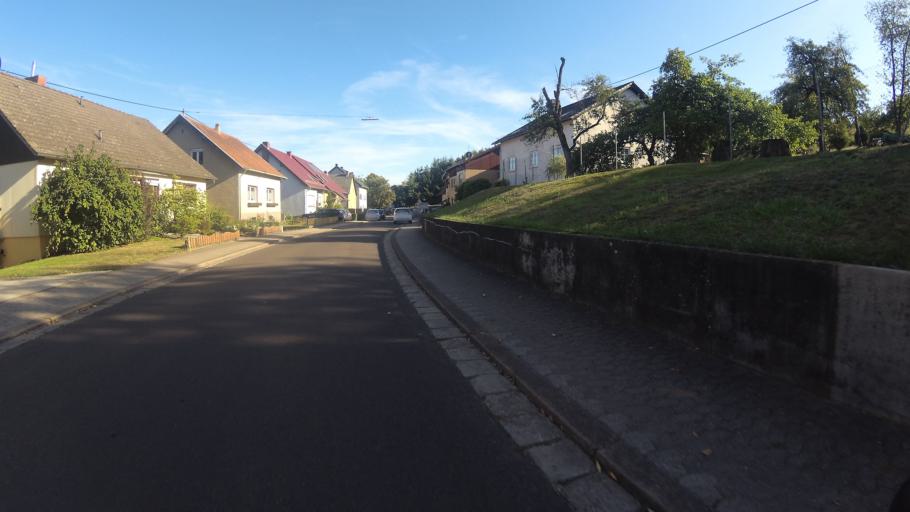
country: DE
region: Saarland
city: Eppelborn
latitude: 49.4368
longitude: 6.9467
